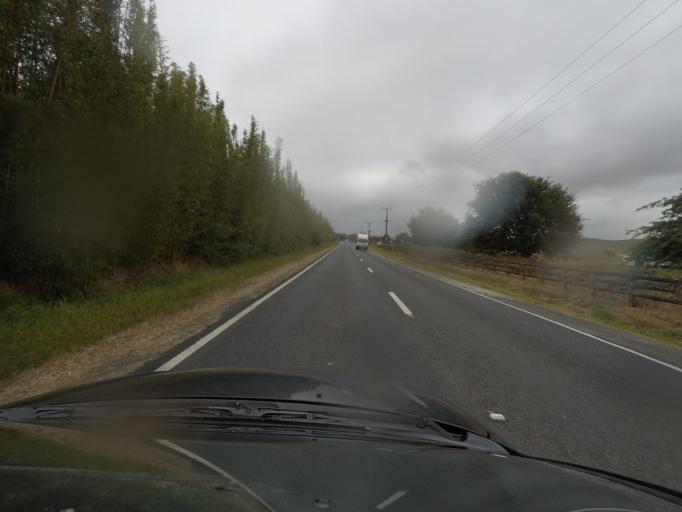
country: NZ
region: Auckland
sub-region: Auckland
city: Warkworth
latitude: -36.3452
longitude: 174.7088
